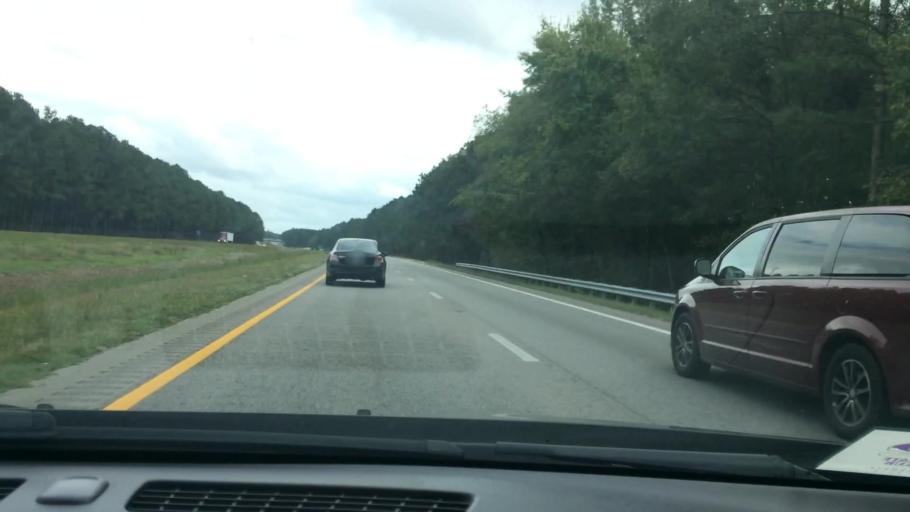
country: US
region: North Carolina
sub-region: Nash County
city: Spring Hope
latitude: 35.7885
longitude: -78.1331
